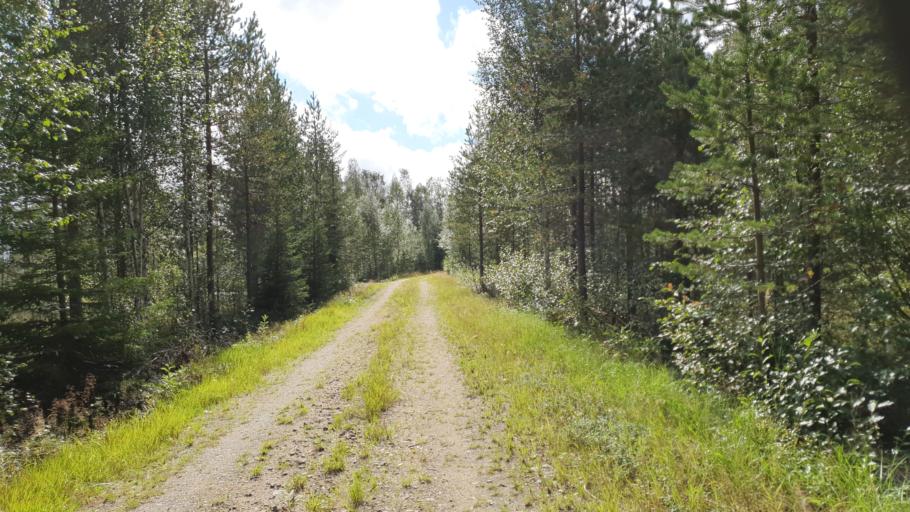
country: FI
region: Kainuu
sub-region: Kehys-Kainuu
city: Kuhmo
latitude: 64.1475
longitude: 29.3555
